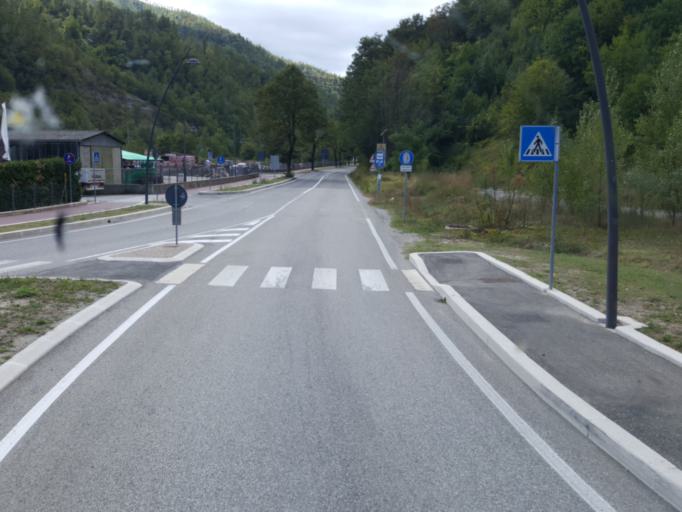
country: IT
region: Emilia-Romagna
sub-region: Forli-Cesena
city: San Piero in Bagno
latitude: 43.8457
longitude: 11.9698
